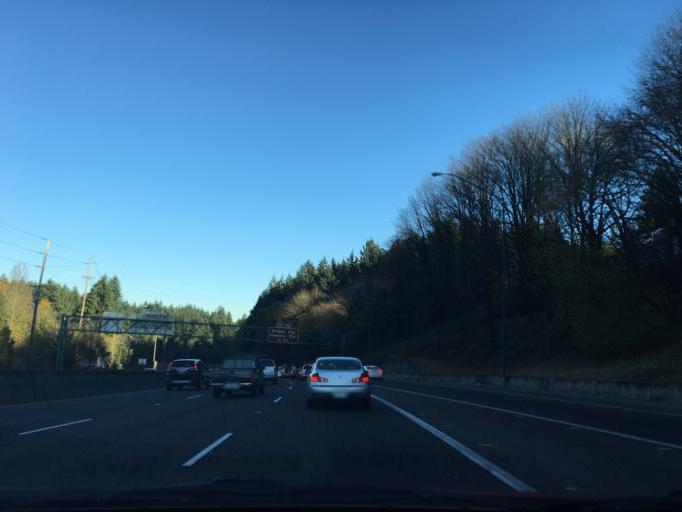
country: US
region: Oregon
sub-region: Washington County
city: West Slope
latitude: 45.5086
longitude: -122.7329
